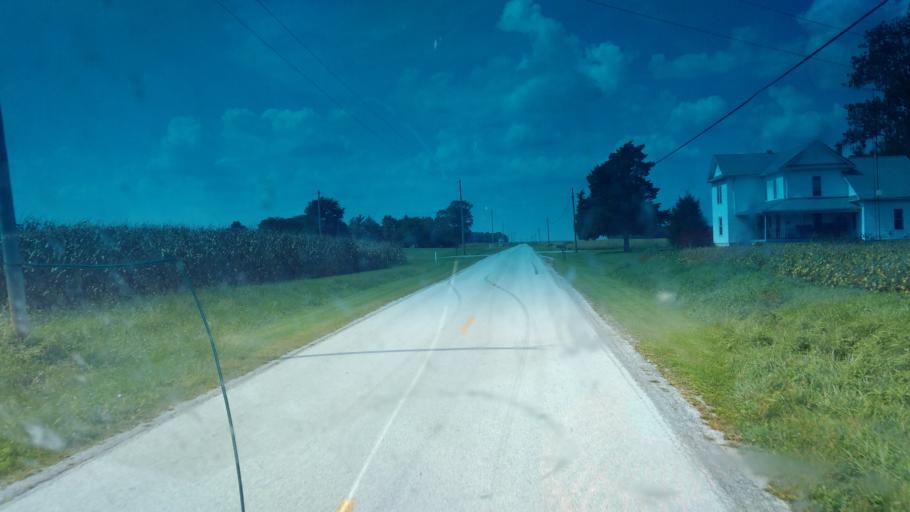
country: US
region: Ohio
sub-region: Hardin County
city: Kenton
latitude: 40.6422
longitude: -83.6721
